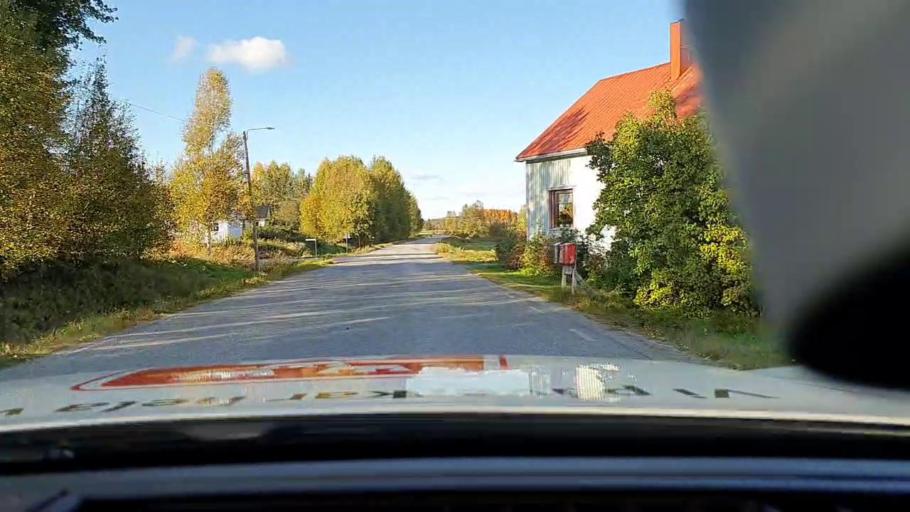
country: SE
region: Norrbotten
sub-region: Pitea Kommun
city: Norrfjarden
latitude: 65.5173
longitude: 21.4950
